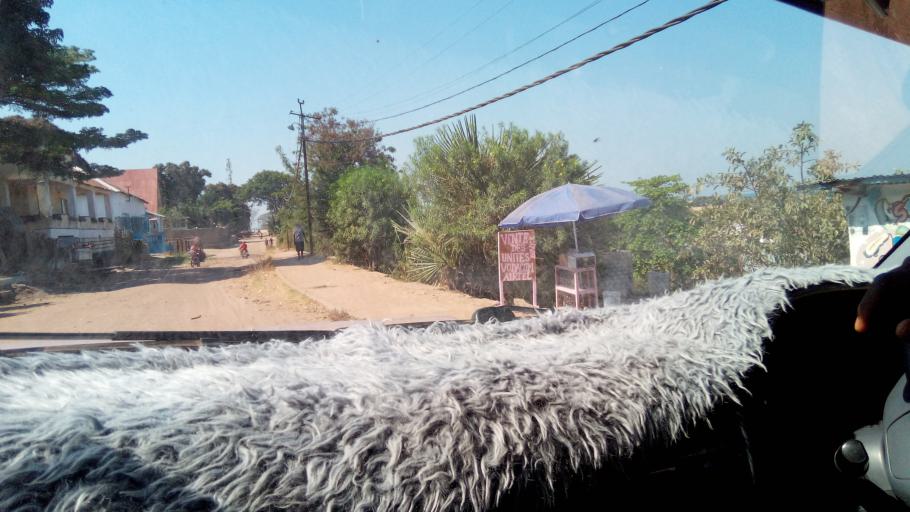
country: CD
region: Katanga
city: Kalemie
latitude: -5.9521
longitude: 29.1966
